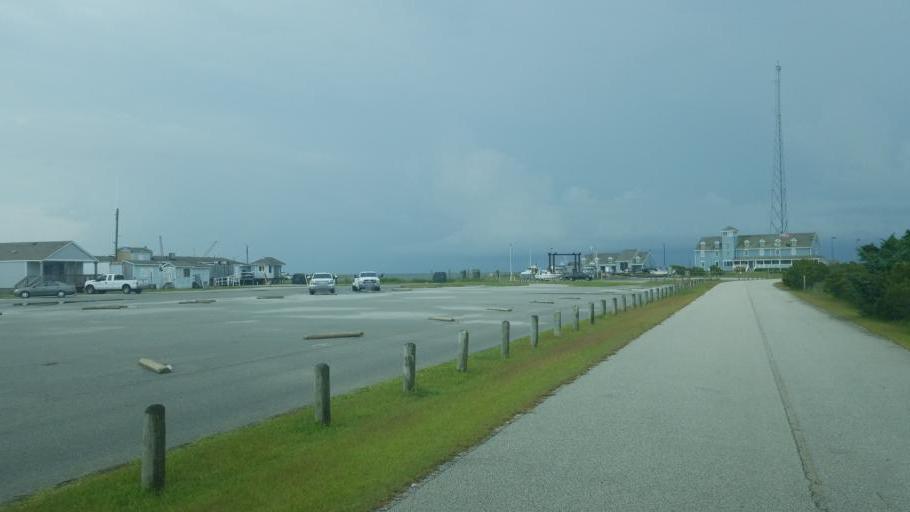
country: US
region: North Carolina
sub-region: Dare County
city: Wanchese
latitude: 35.7980
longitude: -75.5483
